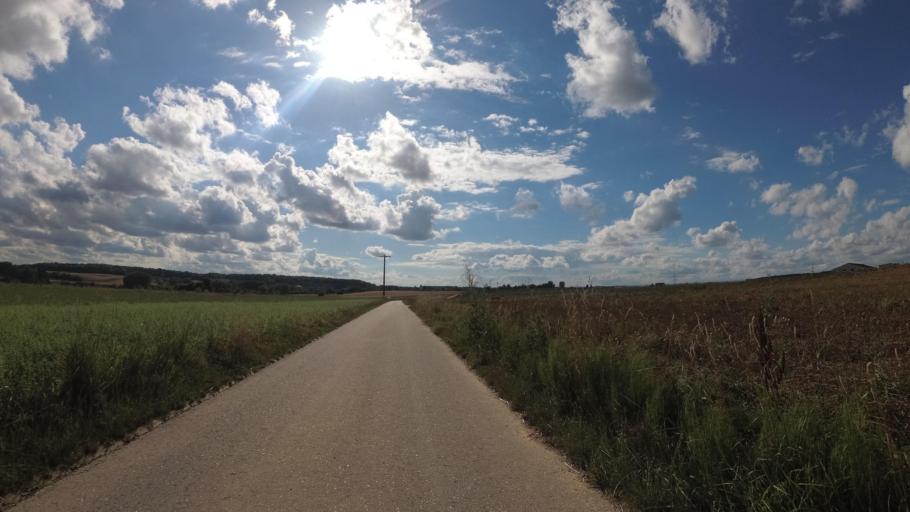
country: DE
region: Baden-Wuerttemberg
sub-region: Regierungsbezirk Stuttgart
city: Neuenstadt am Kocher
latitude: 49.2431
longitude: 9.3262
